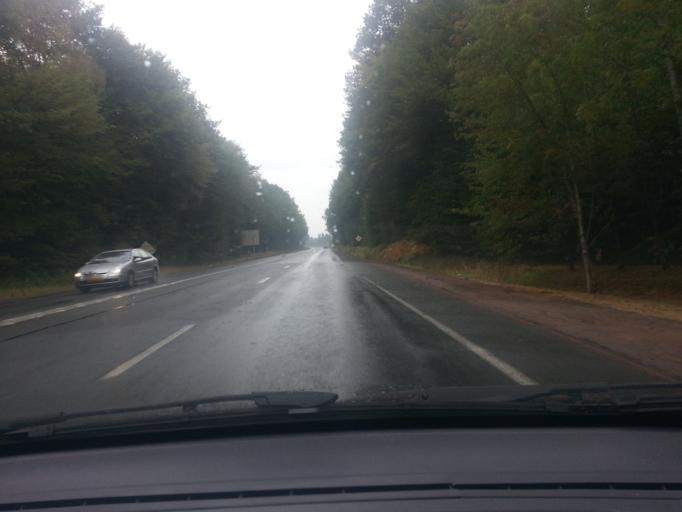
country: FR
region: Bourgogne
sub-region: Departement de Saone-et-Loire
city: Montchanin
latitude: 46.7540
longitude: 4.4861
